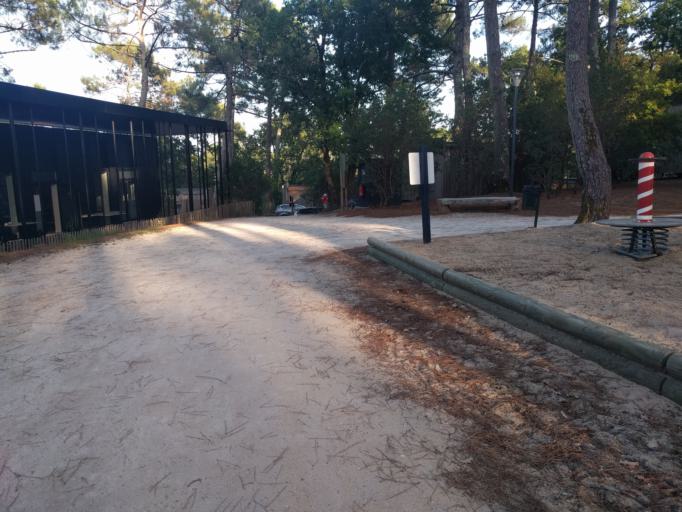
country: FR
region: Aquitaine
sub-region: Departement de la Gironde
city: Ares
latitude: 44.7537
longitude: -1.1883
